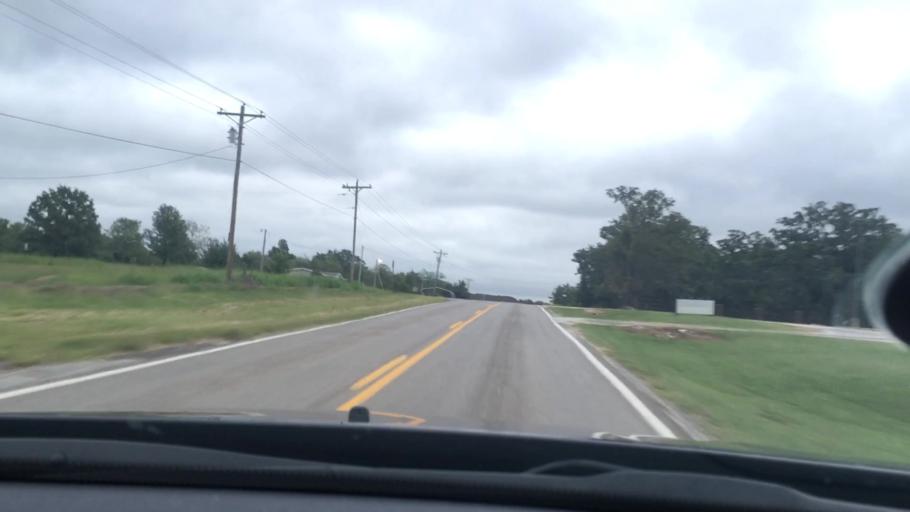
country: US
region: Oklahoma
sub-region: Sequoyah County
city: Vian
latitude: 35.6025
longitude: -95.0129
